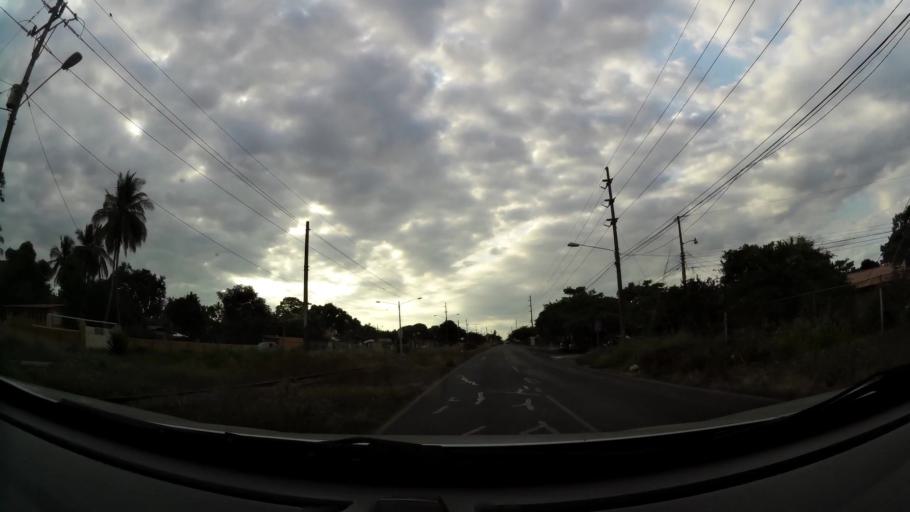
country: CR
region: Puntarenas
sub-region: Canton Central de Puntarenas
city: Chacarita
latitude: 9.9783
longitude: -84.7632
